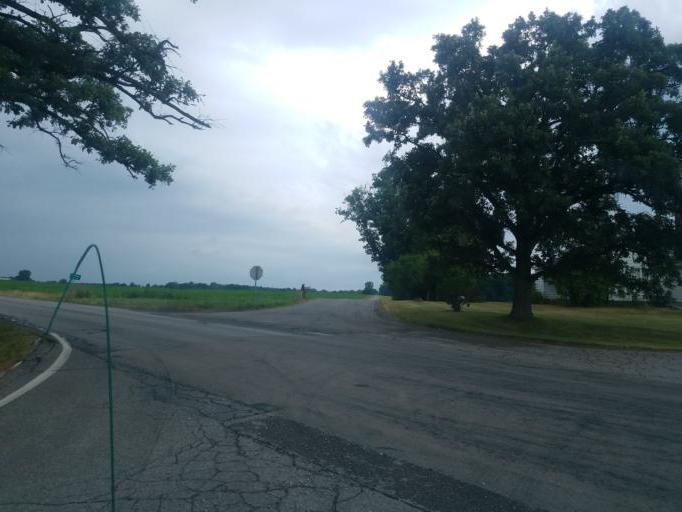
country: US
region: Ohio
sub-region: Defiance County
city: Hicksville
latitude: 41.3248
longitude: -84.8040
